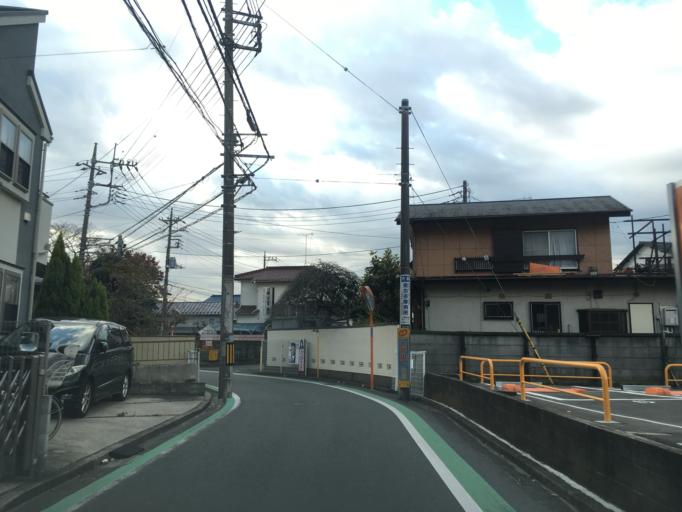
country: JP
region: Tokyo
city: Chofugaoka
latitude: 35.6287
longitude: 139.5876
